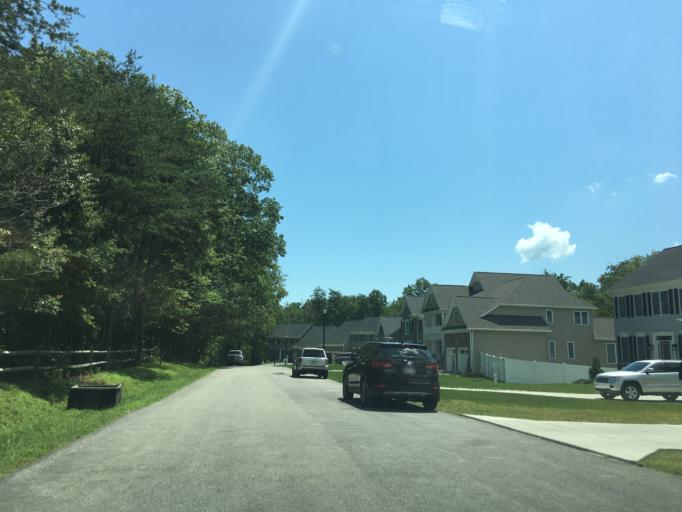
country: US
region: Maryland
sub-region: Anne Arundel County
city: Severna Park
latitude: 39.0846
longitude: -76.5627
